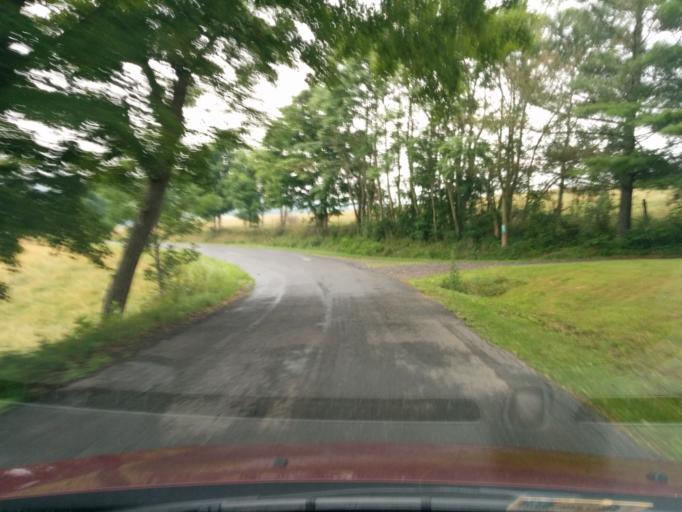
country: US
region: Virginia
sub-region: Rockbridge County
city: East Lexington
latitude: 37.8427
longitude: -79.4275
